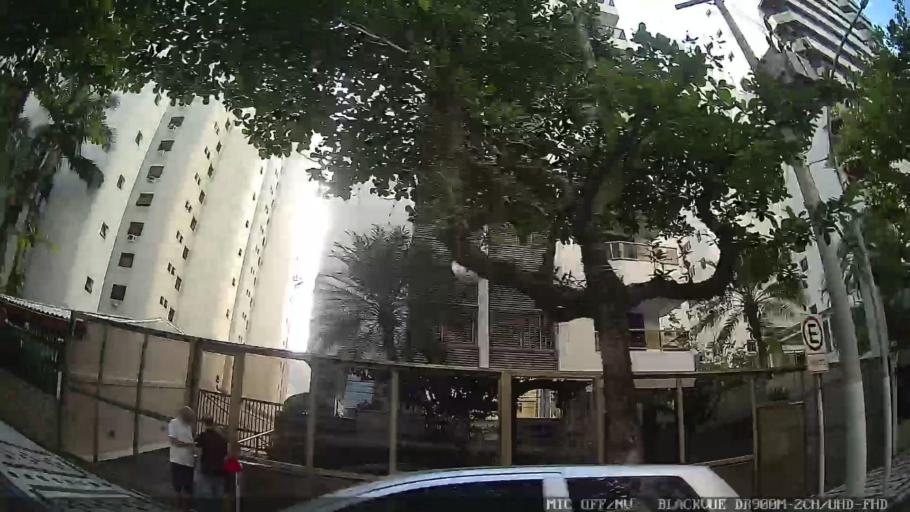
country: BR
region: Sao Paulo
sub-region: Guaruja
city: Guaruja
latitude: -23.9990
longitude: -46.2626
